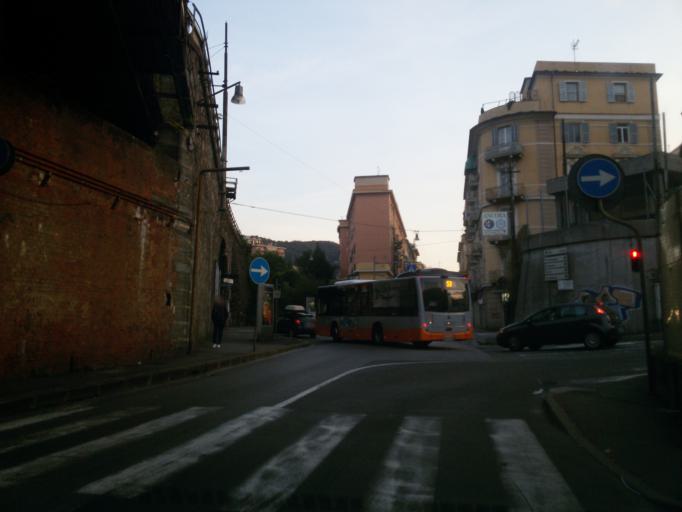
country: IT
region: Liguria
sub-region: Provincia di Genova
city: Genoa
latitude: 44.4367
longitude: 8.8923
